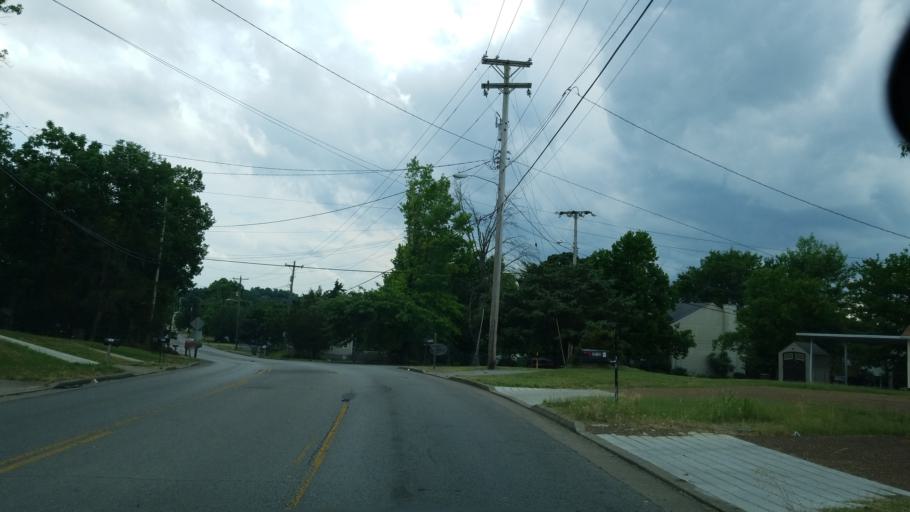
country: US
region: Tennessee
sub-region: Rutherford County
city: La Vergne
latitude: 36.0763
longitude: -86.6084
